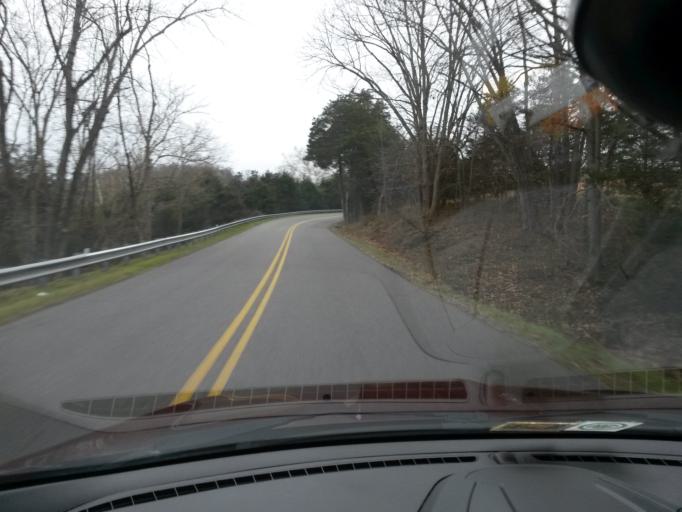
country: US
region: Virginia
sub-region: Rockbridge County
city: East Lexington
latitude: 37.7893
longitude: -79.4009
